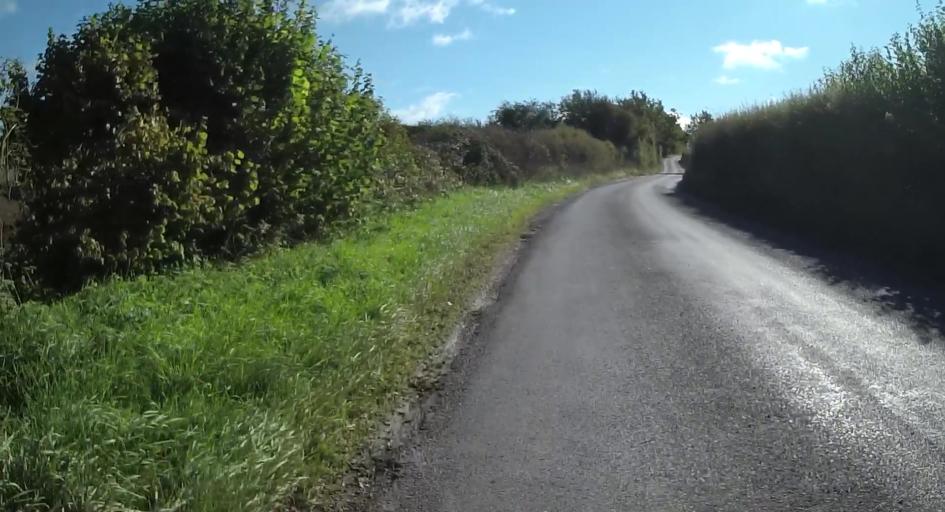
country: GB
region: England
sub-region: Hampshire
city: Hook
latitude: 51.2576
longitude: -0.9888
